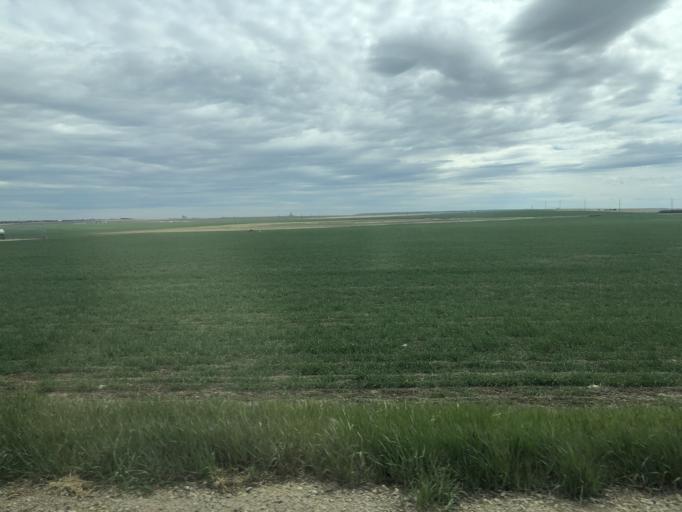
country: CA
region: Alberta
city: Vulcan
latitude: 50.3715
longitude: -113.3231
